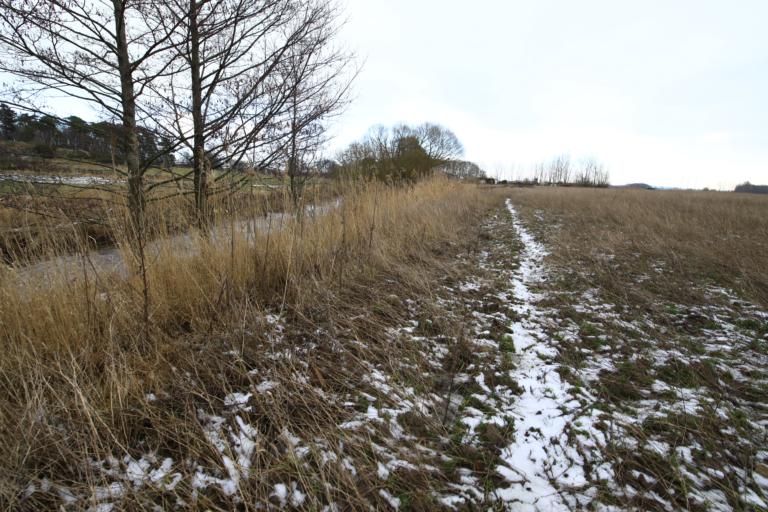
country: SE
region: Halland
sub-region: Varbergs Kommun
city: Varberg
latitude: 57.1285
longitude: 12.3052
